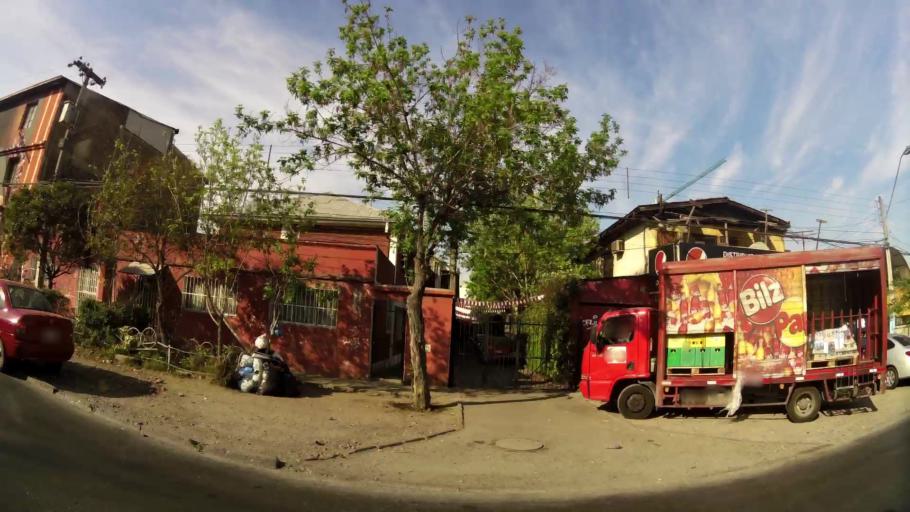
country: CL
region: Santiago Metropolitan
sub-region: Provincia de Santiago
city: Santiago
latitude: -33.5017
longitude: -70.6615
